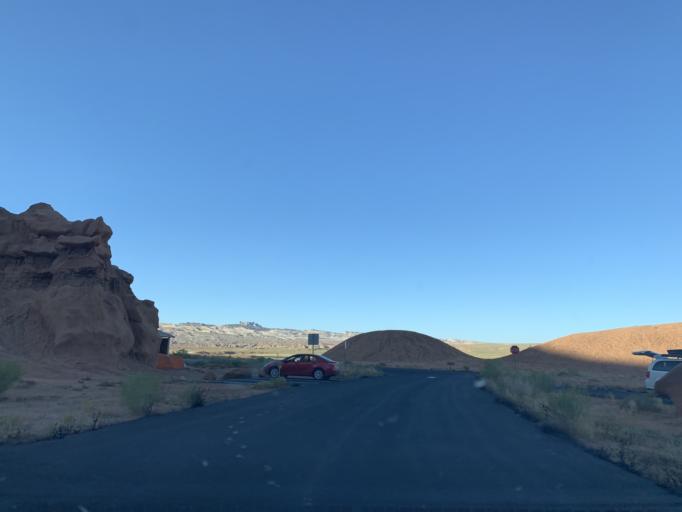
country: US
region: Utah
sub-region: Emery County
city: Ferron
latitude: 38.5732
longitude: -110.7147
